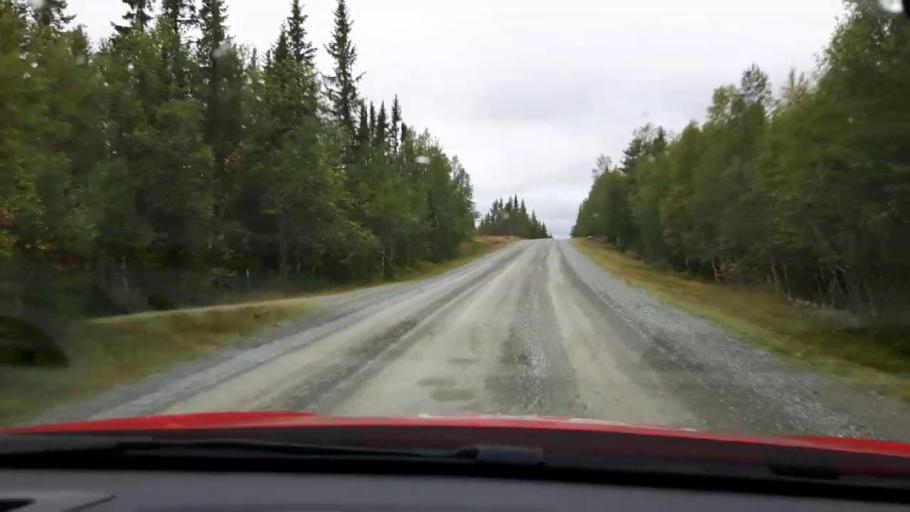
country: SE
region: Jaemtland
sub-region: Bergs Kommun
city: Hoverberg
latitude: 62.9099
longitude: 14.0849
